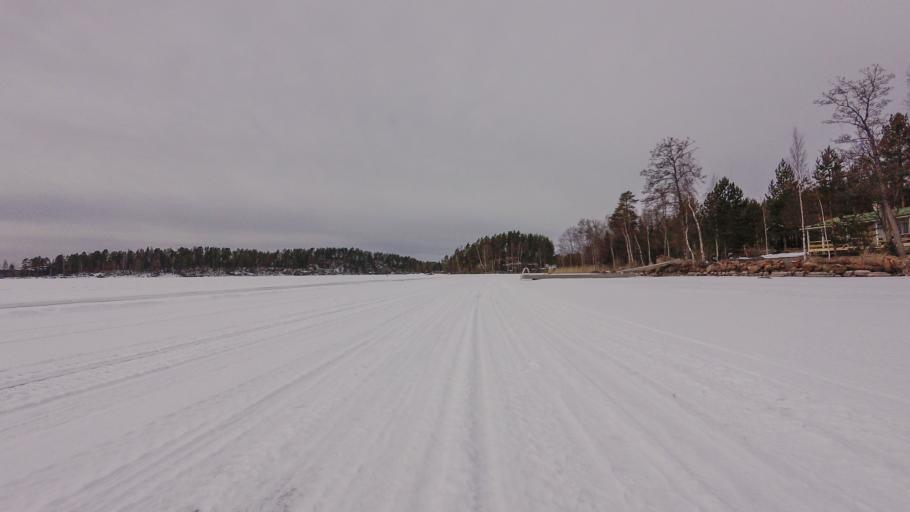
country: FI
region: Southern Savonia
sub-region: Savonlinna
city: Rantasalmi
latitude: 62.1140
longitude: 28.3300
